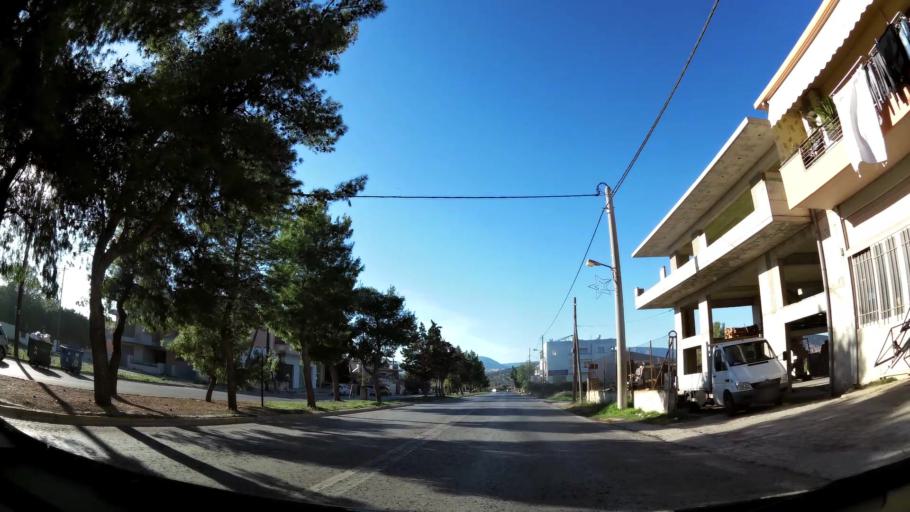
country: GR
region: Attica
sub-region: Nomarchia Anatolikis Attikis
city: Kalyvia Thorikou
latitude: 37.8447
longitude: 23.9266
